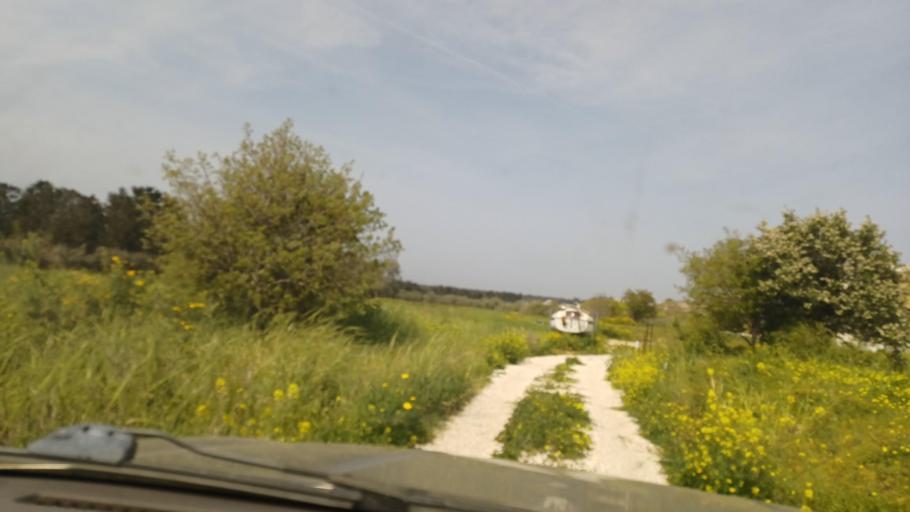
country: CY
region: Pafos
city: Paphos
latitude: 34.7498
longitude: 32.4638
